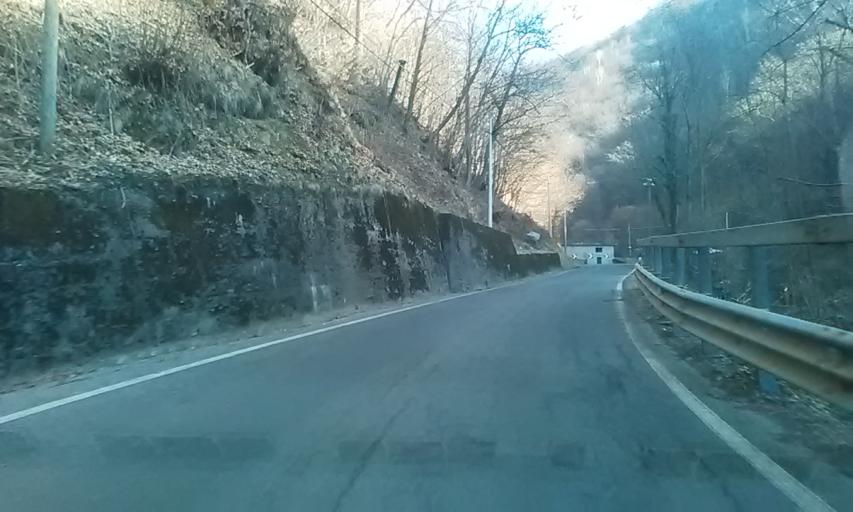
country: IT
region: Piedmont
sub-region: Provincia di Vercelli
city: Quarona
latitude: 45.7663
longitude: 8.2812
